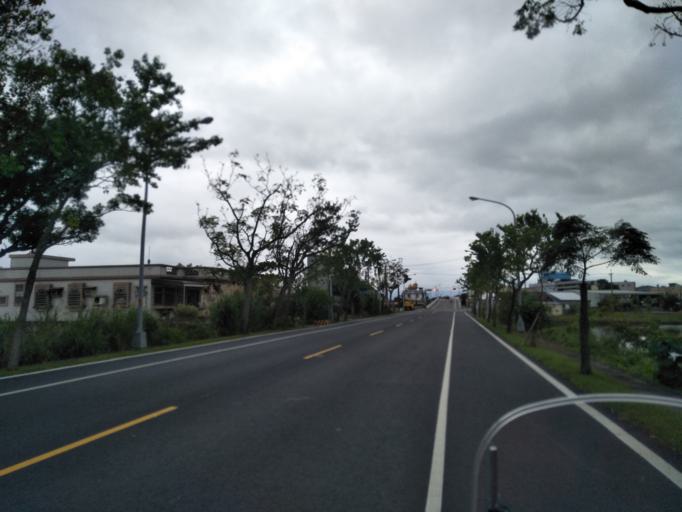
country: TW
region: Taiwan
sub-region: Yilan
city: Yilan
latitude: 24.8119
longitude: 121.7927
